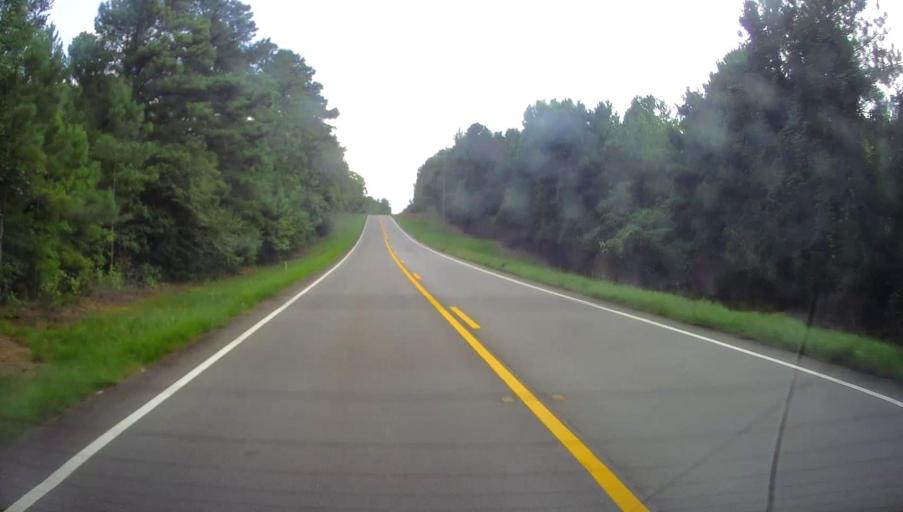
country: US
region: Georgia
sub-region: Monroe County
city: Forsyth
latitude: 32.9840
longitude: -83.9518
